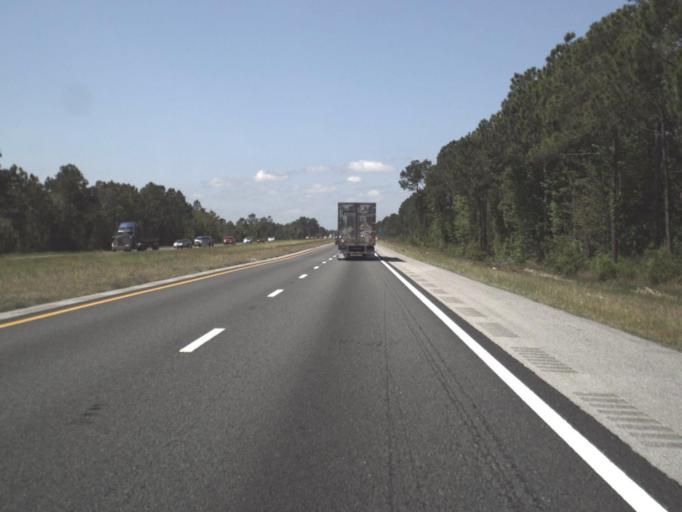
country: US
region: Florida
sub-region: Santa Rosa County
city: Bagdad
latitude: 30.5453
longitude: -87.0636
